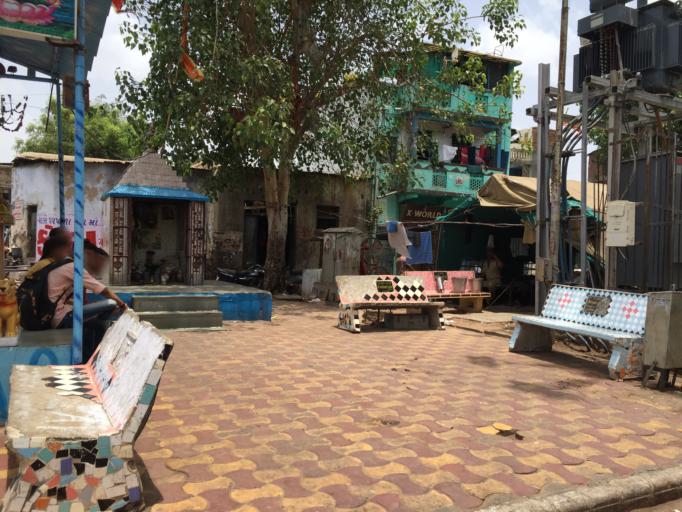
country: IN
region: Gujarat
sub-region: Ahmadabad
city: Ahmedabad
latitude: 23.0351
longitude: 72.5847
